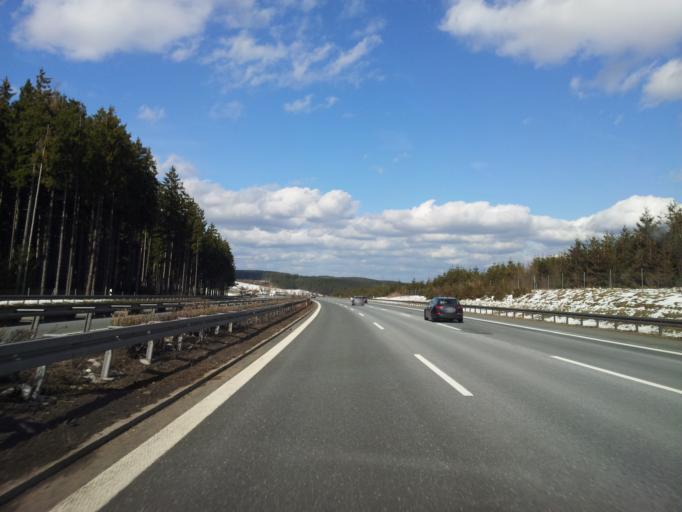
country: DE
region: Bavaria
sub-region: Upper Franconia
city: Leupoldsgrun
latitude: 50.2484
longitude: 11.7896
